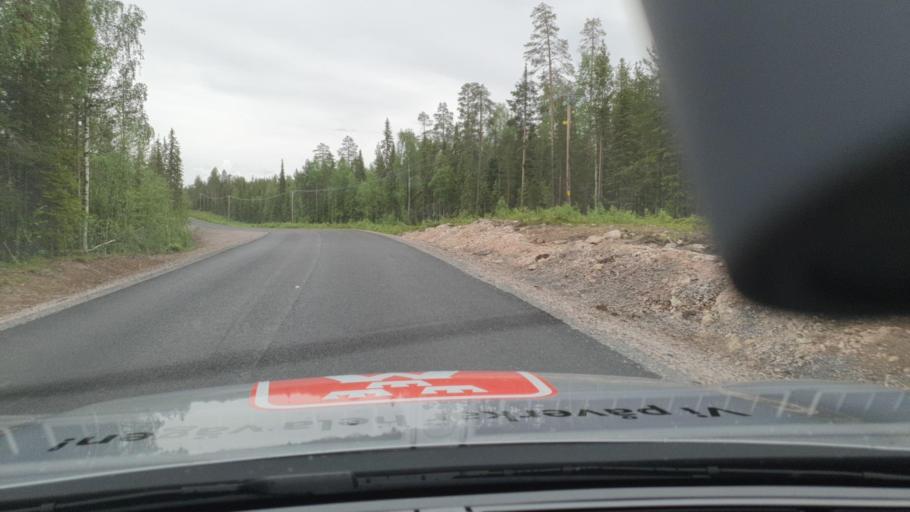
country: SE
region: Norrbotten
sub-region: Overtornea Kommun
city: OEvertornea
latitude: 66.6550
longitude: 23.2273
